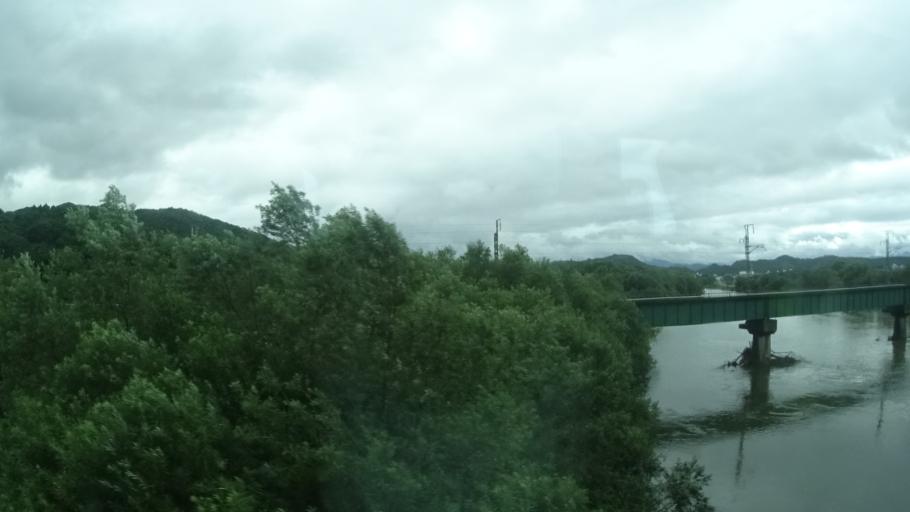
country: JP
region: Niigata
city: Murakami
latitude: 38.2367
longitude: 139.4588
